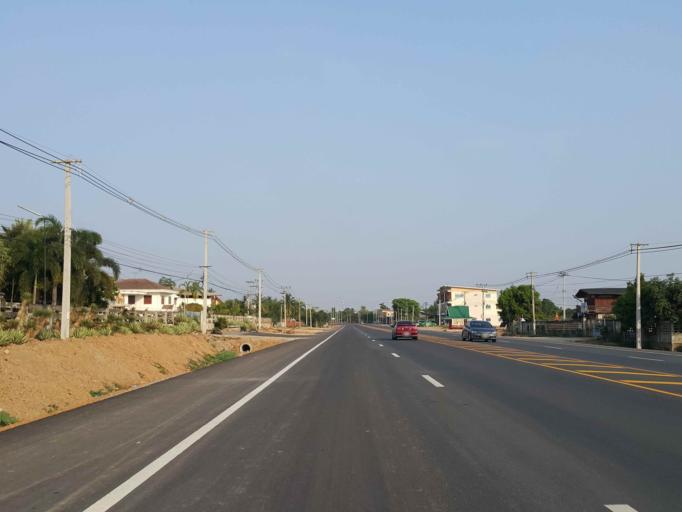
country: TH
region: Sukhothai
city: Sawankhalok
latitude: 17.3057
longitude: 99.8202
